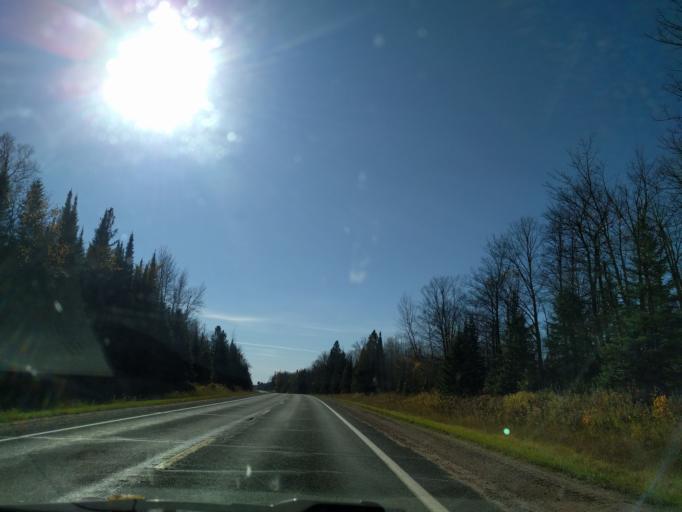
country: US
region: Michigan
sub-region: Iron County
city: Crystal Falls
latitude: 46.1662
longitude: -88.0733
